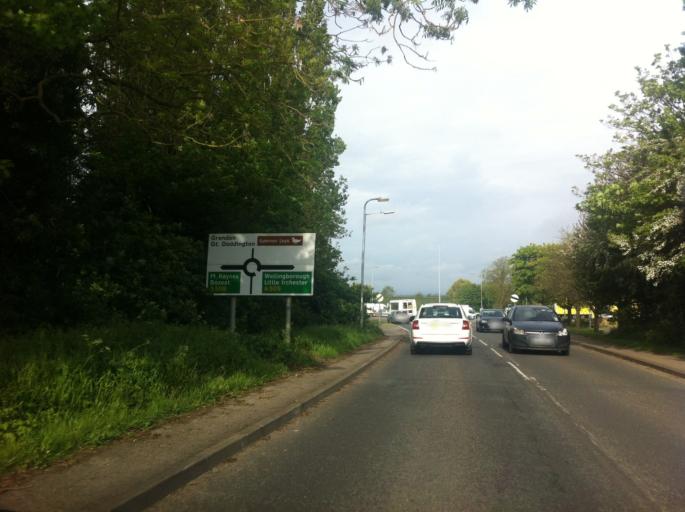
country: GB
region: England
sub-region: Northamptonshire
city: Bozeat
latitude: 52.2579
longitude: -0.6765
